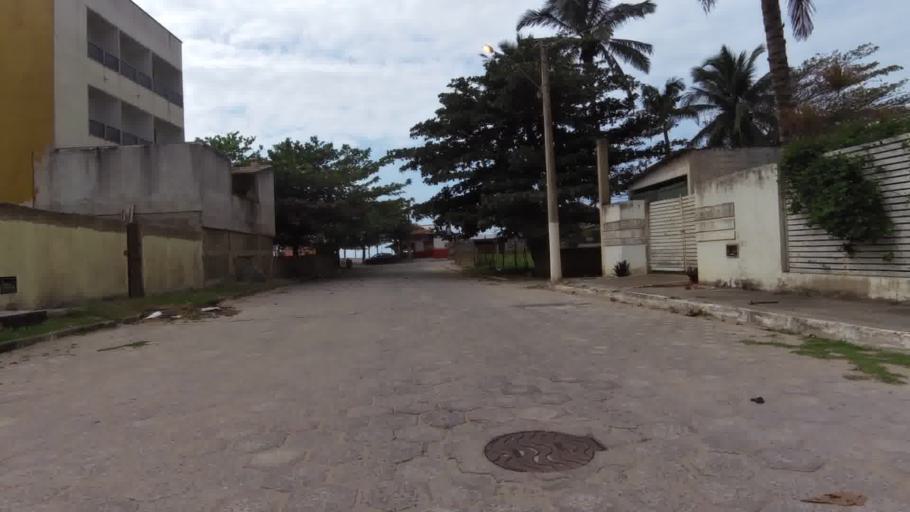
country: BR
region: Espirito Santo
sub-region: Marataizes
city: Marataizes
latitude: -21.0341
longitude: -40.8140
